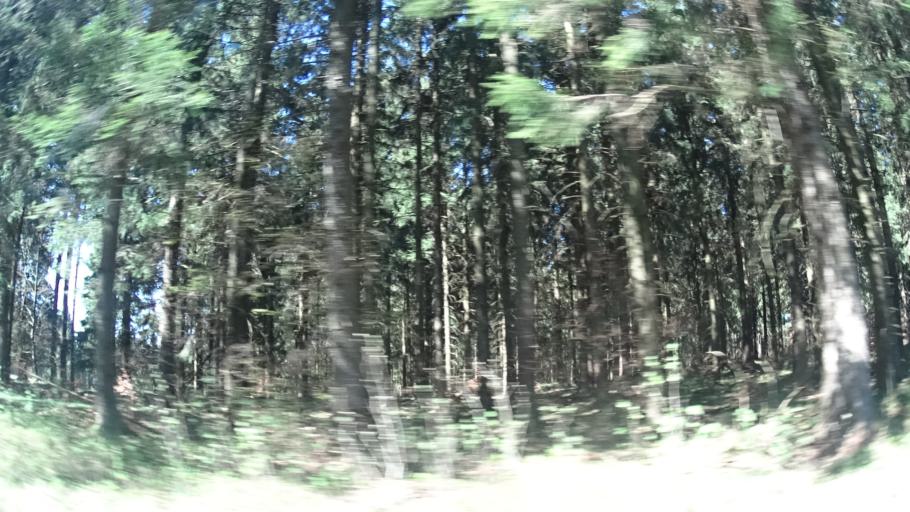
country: DE
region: Thuringia
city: Frauenwald
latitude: 50.5636
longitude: 10.8600
